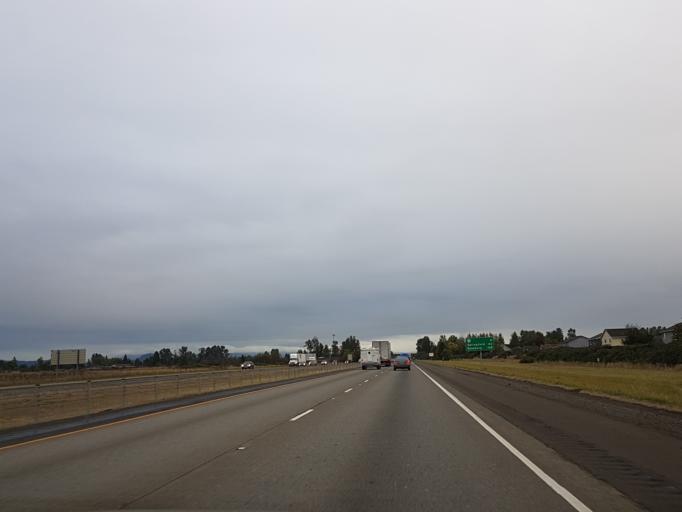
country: US
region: Oregon
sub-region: Linn County
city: Albany
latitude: 44.6181
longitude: -123.0623
